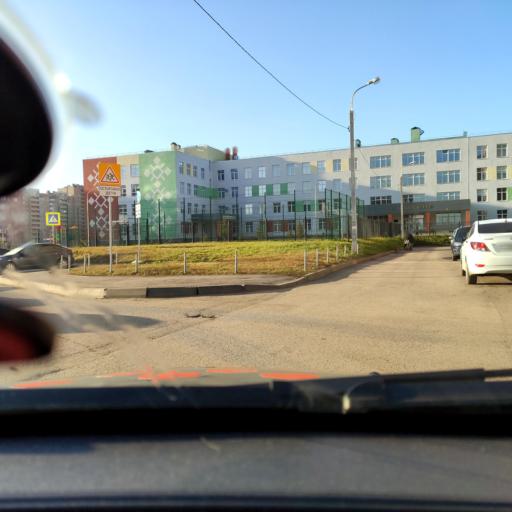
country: RU
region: Bashkortostan
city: Mikhaylovka
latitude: 54.7154
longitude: 55.8410
